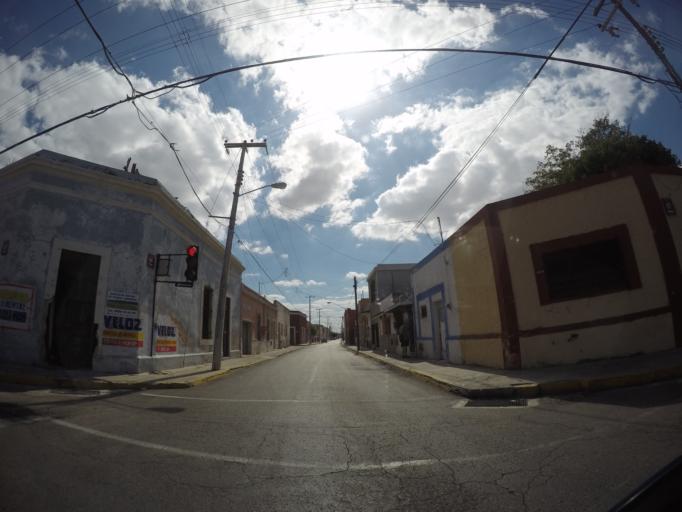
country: MX
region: Yucatan
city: Merida
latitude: 20.9760
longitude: -89.6258
